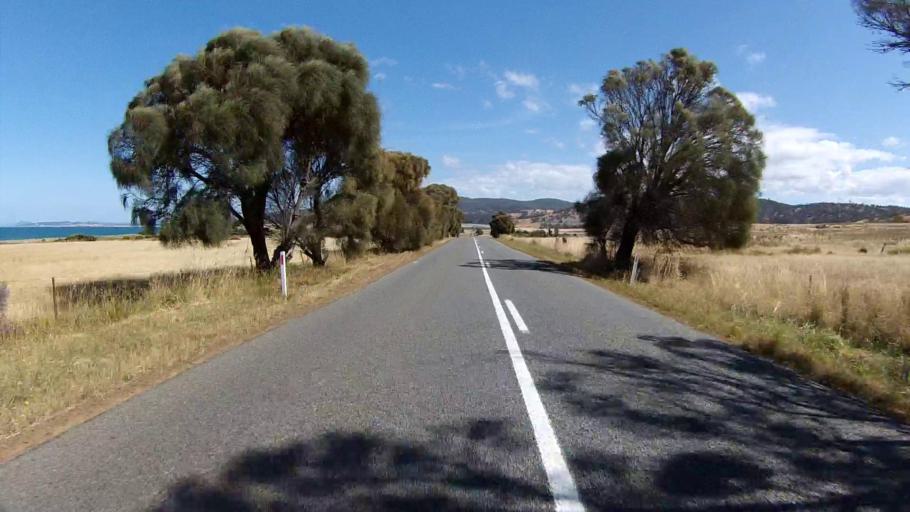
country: AU
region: Tasmania
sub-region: Sorell
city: Sorell
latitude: -42.1946
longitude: 148.0561
